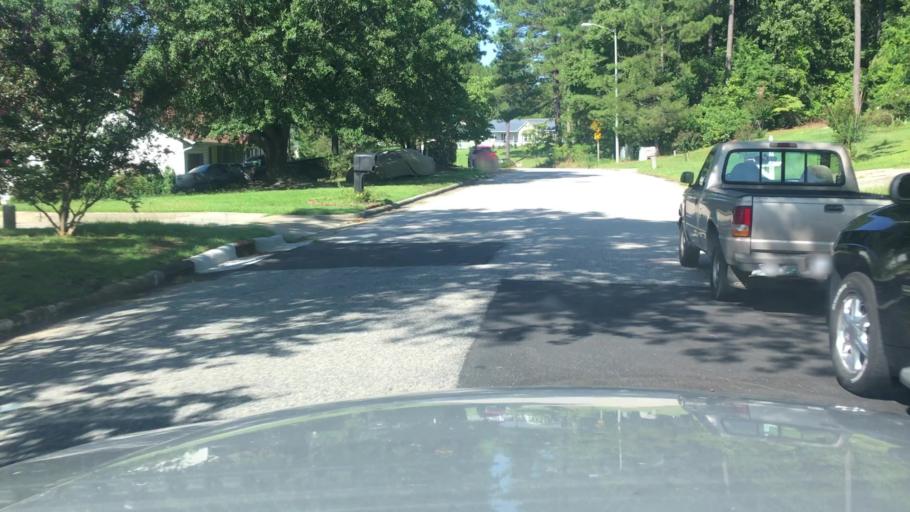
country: US
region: North Carolina
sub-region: Cumberland County
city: Fayetteville
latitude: 35.1082
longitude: -78.9052
